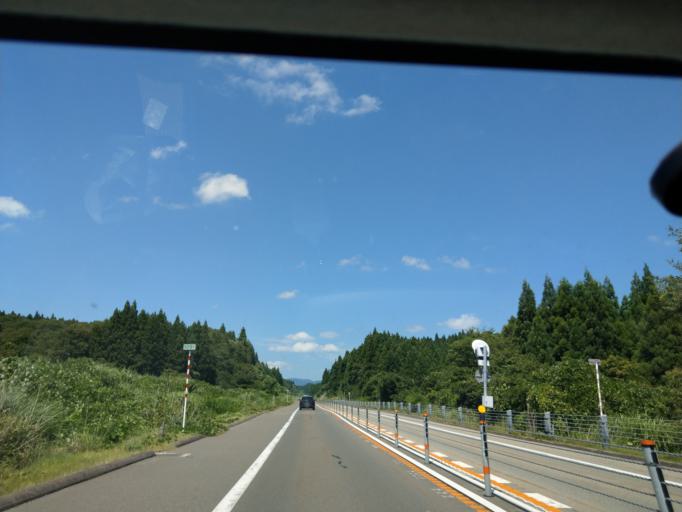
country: JP
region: Akita
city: Akita
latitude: 39.6864
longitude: 140.1857
